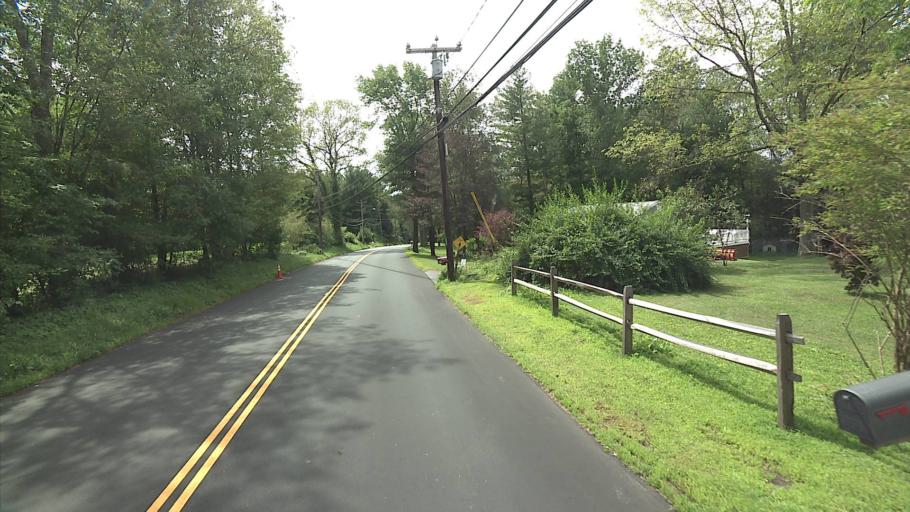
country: US
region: Connecticut
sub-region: Windham County
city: South Woodstock
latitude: 41.9434
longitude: -72.0686
